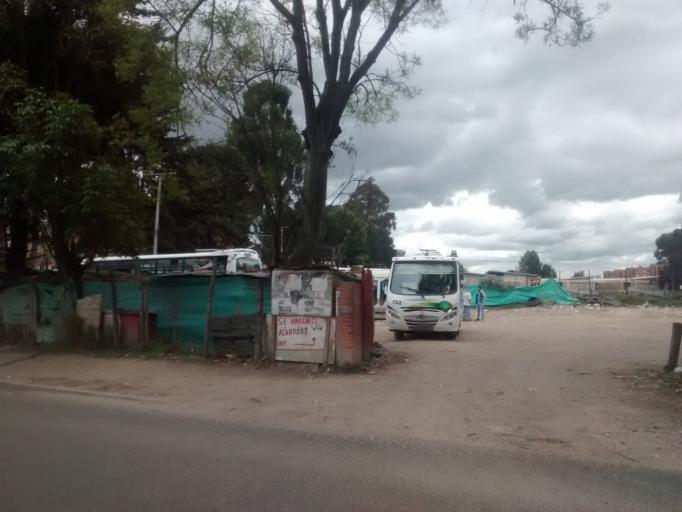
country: CO
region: Cundinamarca
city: Cota
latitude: 4.7495
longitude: -74.1054
